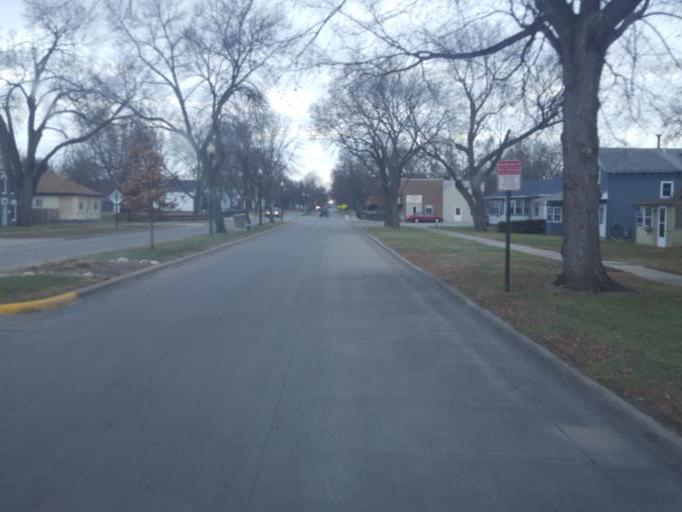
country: US
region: South Dakota
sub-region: Yankton County
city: Yankton
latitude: 42.8762
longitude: -97.3921
